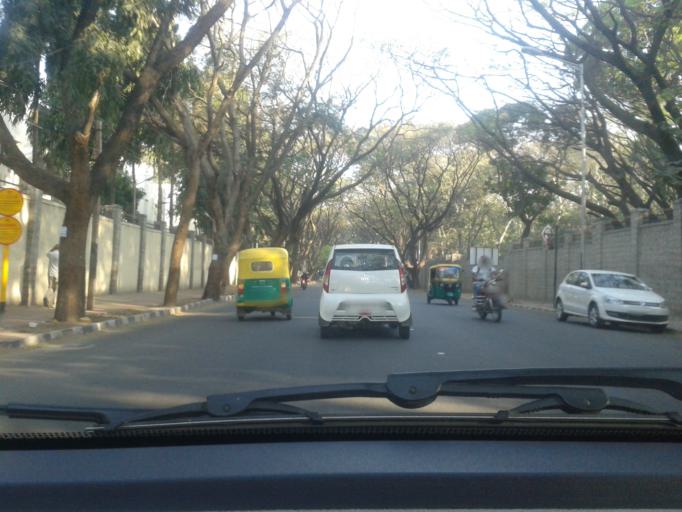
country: IN
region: Karnataka
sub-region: Bangalore Urban
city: Bangalore
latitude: 13.0238
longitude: 77.5721
